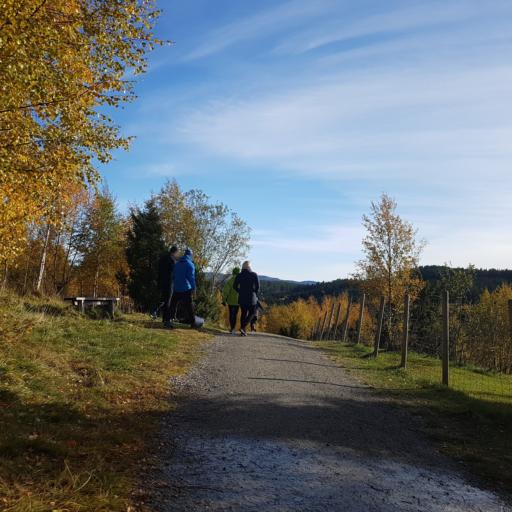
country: NO
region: Sor-Trondelag
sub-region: Trondheim
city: Trondheim
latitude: 63.4213
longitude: 10.3075
